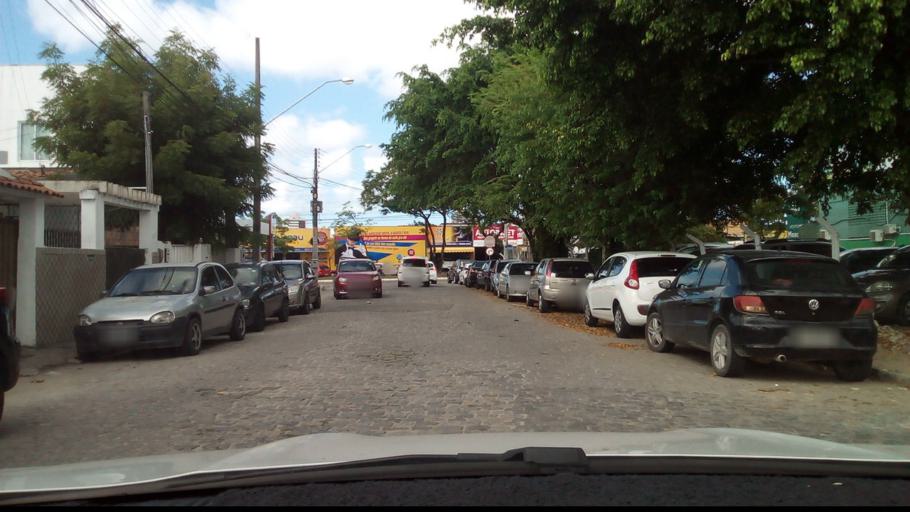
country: BR
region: Paraiba
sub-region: Joao Pessoa
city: Joao Pessoa
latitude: -7.1294
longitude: -34.8591
